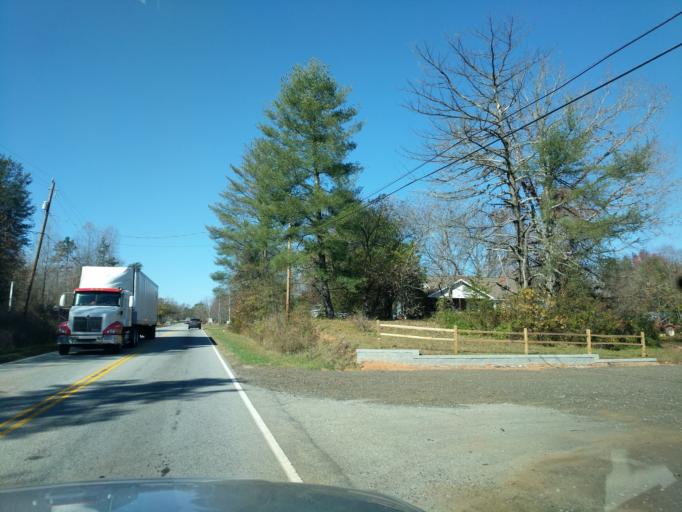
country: US
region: South Carolina
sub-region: Greenville County
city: Taylors
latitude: 34.9847
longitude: -82.3359
